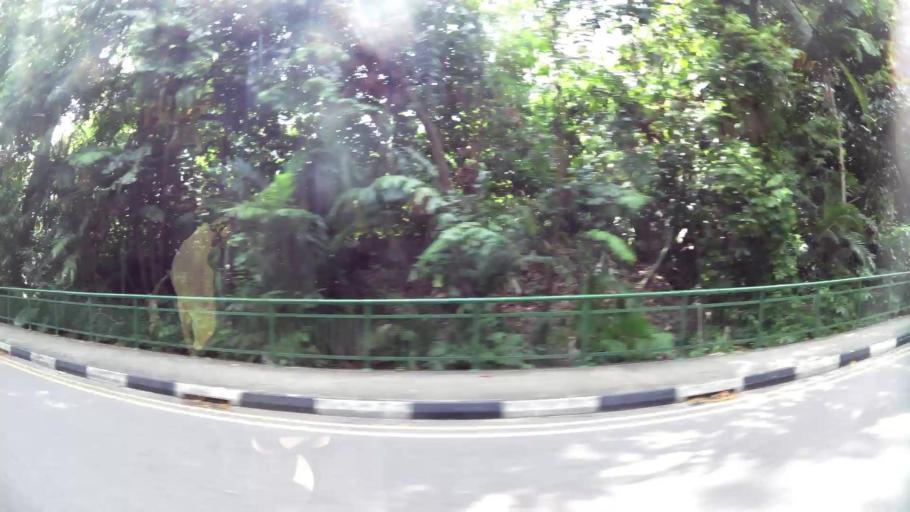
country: SG
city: Singapore
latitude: 1.3115
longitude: 103.8331
